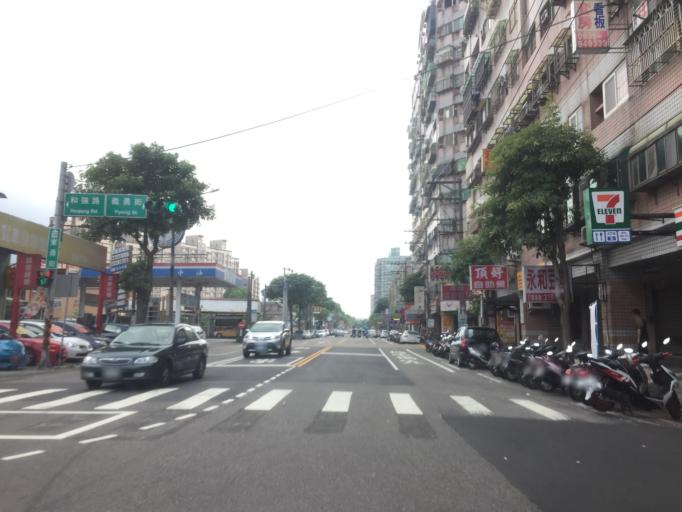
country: TW
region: Taiwan
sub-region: Taoyuan
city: Taoyuan
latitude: 24.9632
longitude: 121.3068
